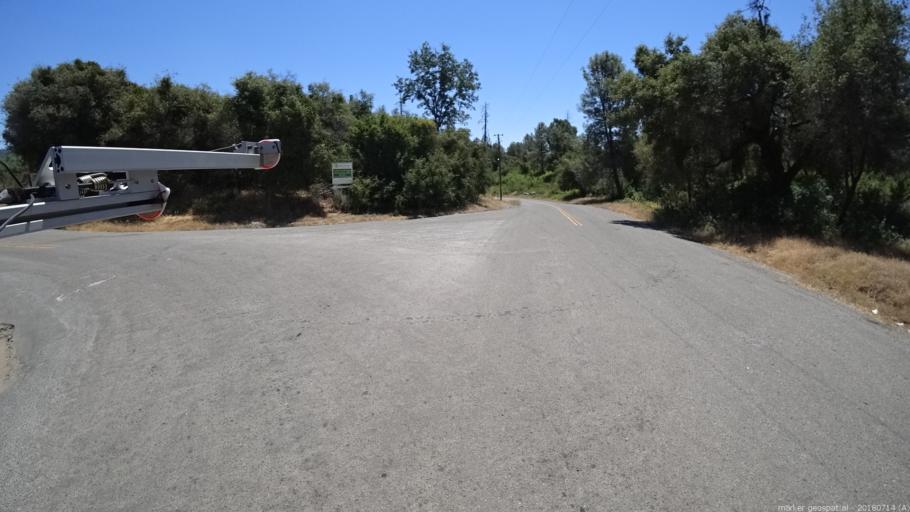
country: US
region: California
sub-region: Madera County
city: Ahwahnee
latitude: 37.3970
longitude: -119.7054
